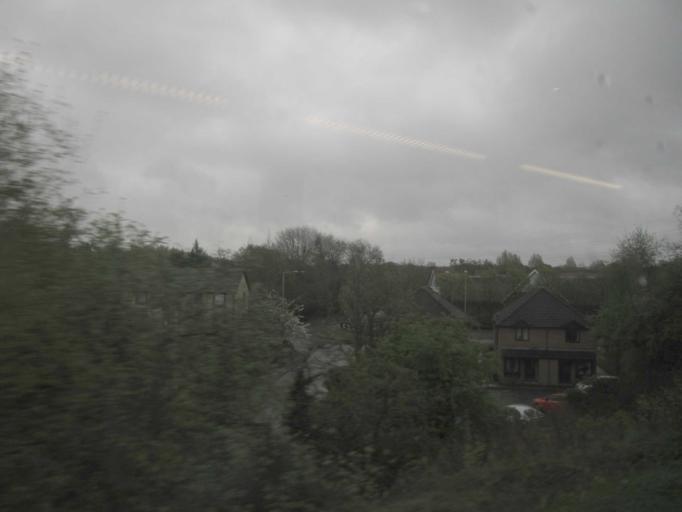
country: GB
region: England
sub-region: Wokingham
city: Wokingham
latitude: 51.4038
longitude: -0.8390
